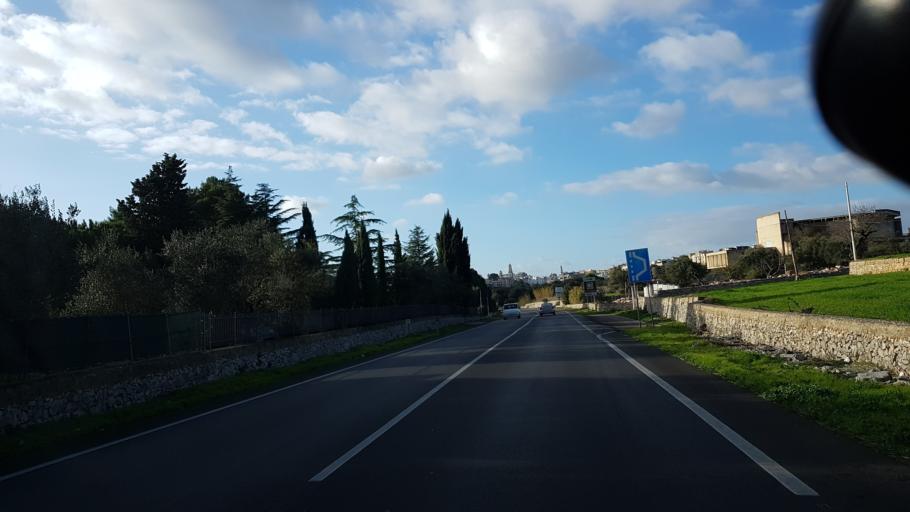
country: IT
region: Apulia
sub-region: Provincia di Bari
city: Putignano
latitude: 40.8441
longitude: 17.1391
